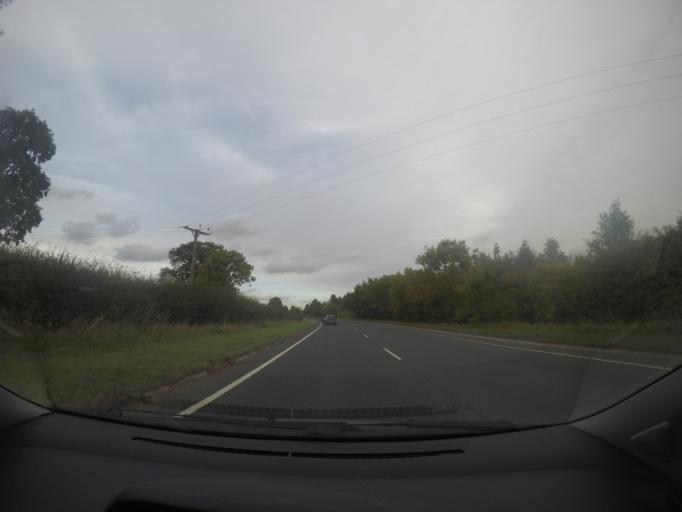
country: GB
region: England
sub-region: North Yorkshire
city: Riccall
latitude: 53.8502
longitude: -1.0504
